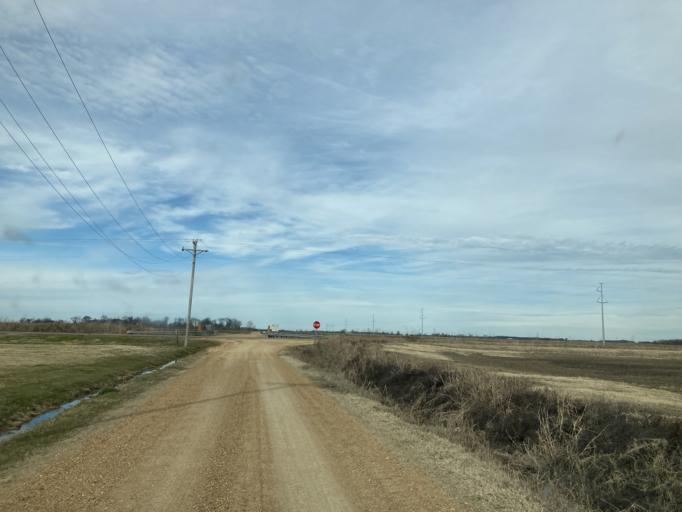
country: US
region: Mississippi
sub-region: Humphreys County
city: Belzoni
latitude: 33.1668
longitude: -90.5553
